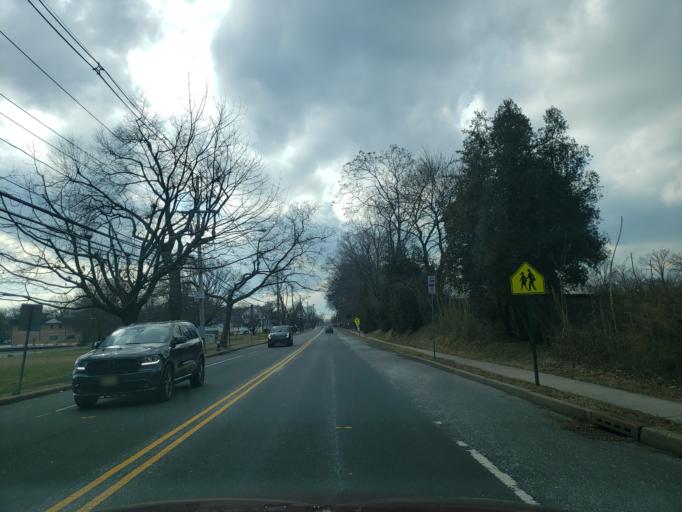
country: US
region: New Jersey
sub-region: Union County
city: Springfield
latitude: 40.6946
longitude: -74.3275
